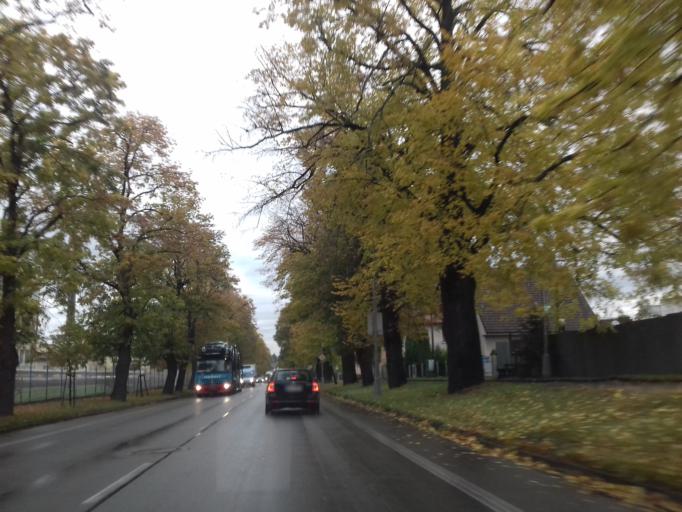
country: CZ
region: Pardubicky
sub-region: Okres Pardubice
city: Vysoke Myto
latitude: 49.9581
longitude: 16.1494
